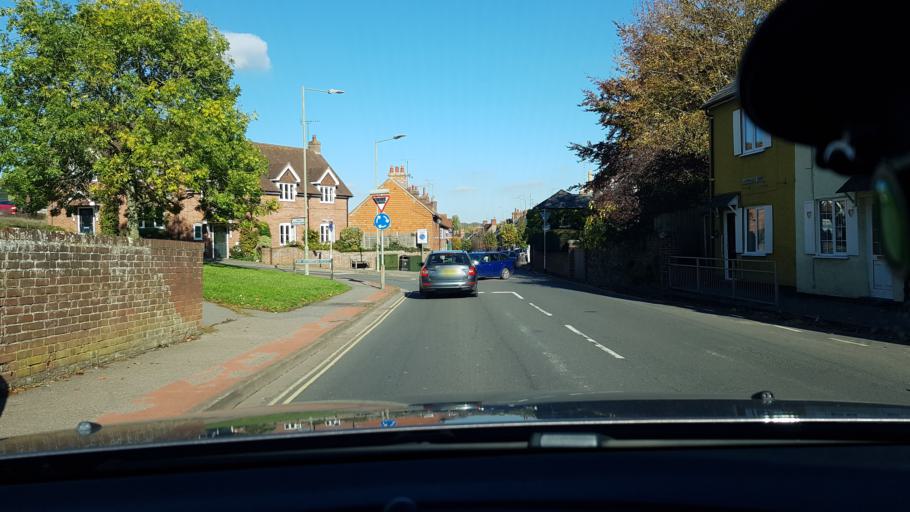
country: GB
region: England
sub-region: West Berkshire
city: Hungerford
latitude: 51.4115
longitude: -1.5174
